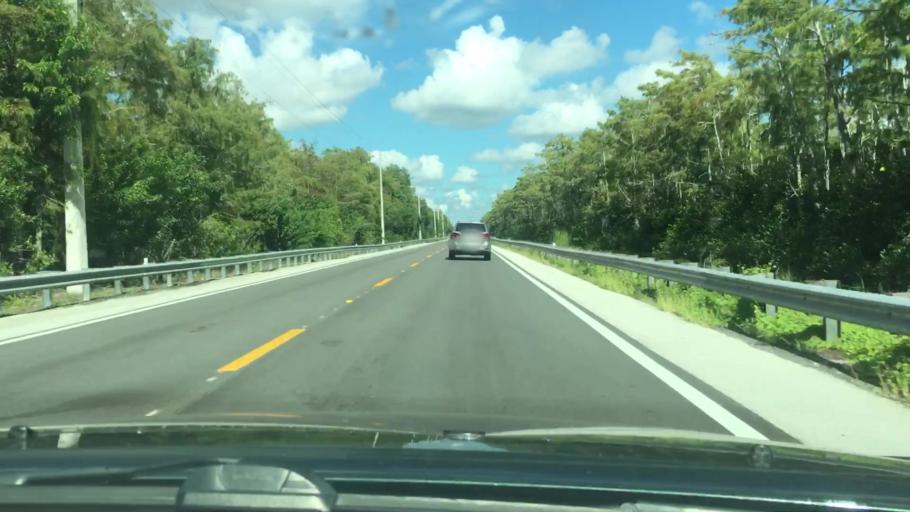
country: US
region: Florida
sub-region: Miami-Dade County
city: Kendall West
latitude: 25.7996
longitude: -80.8670
